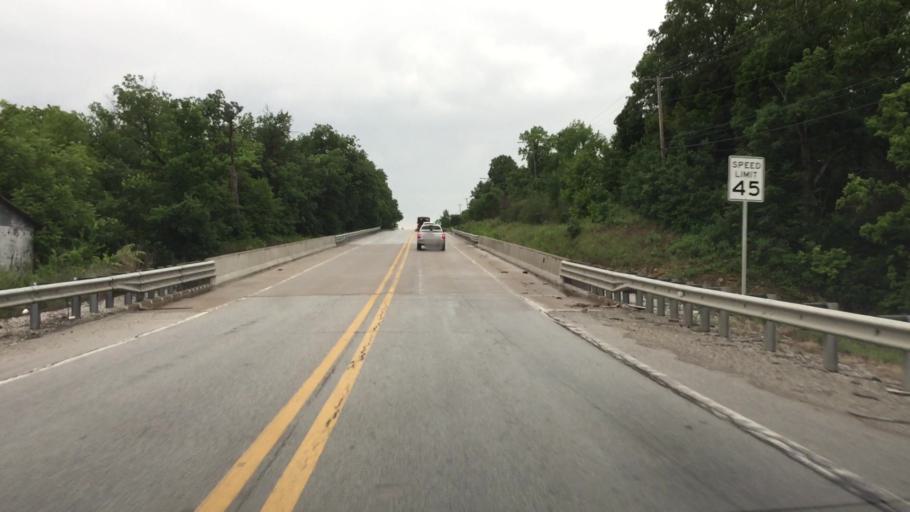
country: US
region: Illinois
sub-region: Hancock County
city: Hamilton
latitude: 40.3864
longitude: -91.3405
